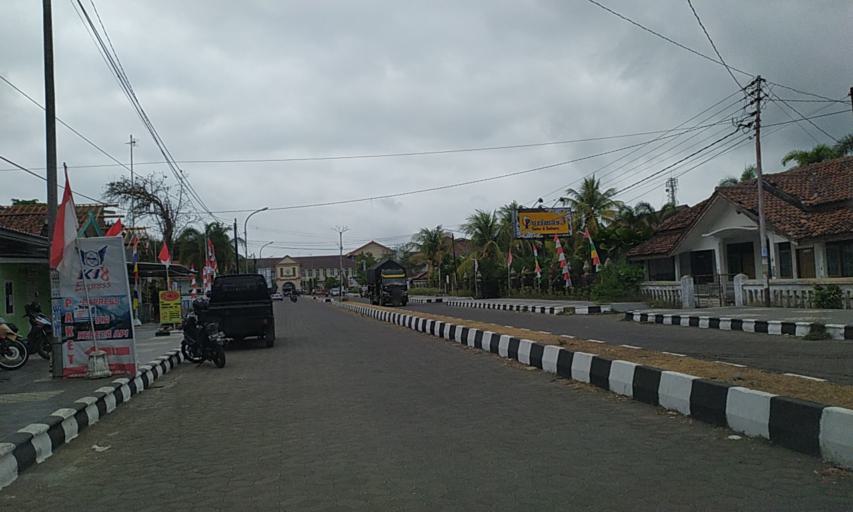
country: ID
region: Central Java
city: Karangbadar Kidul
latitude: -7.7361
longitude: 109.0078
